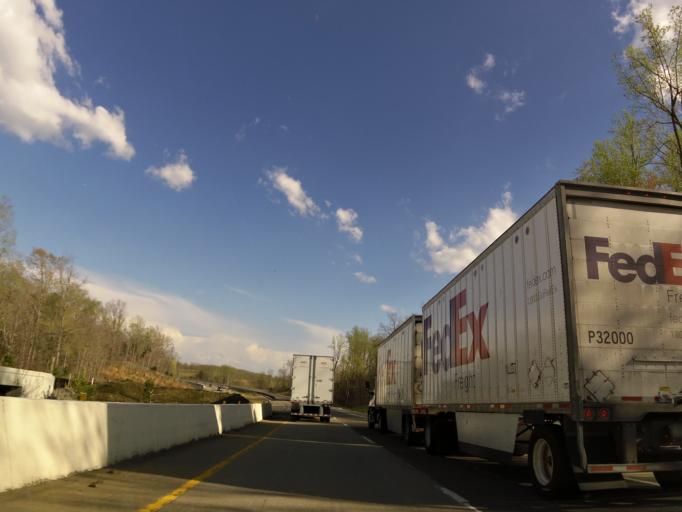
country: US
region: Tennessee
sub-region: Williamson County
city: Thompson's Station
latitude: 35.8298
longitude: -87.0586
